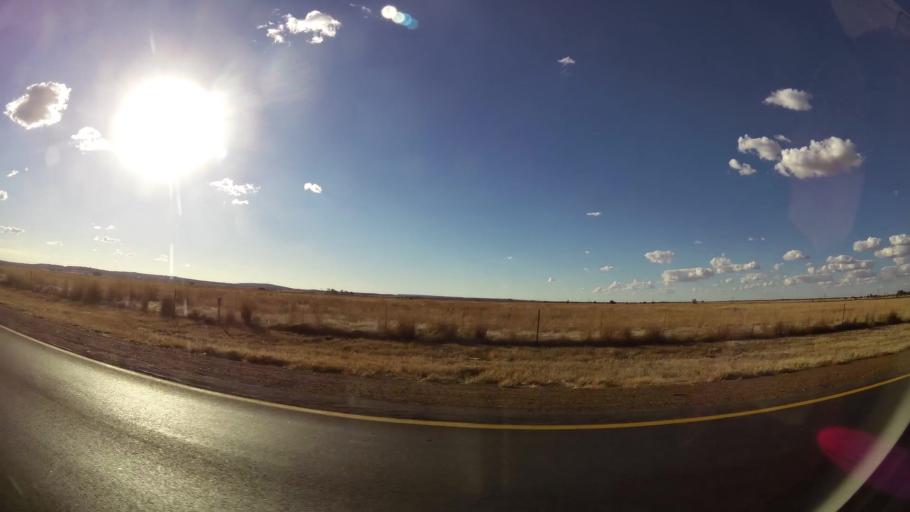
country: ZA
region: North-West
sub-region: Dr Kenneth Kaunda District Municipality
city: Stilfontein
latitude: -26.8438
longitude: 26.7341
